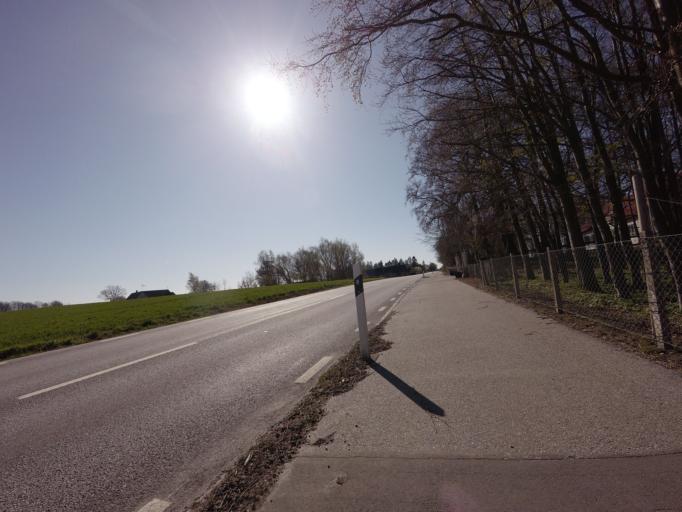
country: SE
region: Skane
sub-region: Malmo
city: Oxie
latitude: 55.4846
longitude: 13.1250
